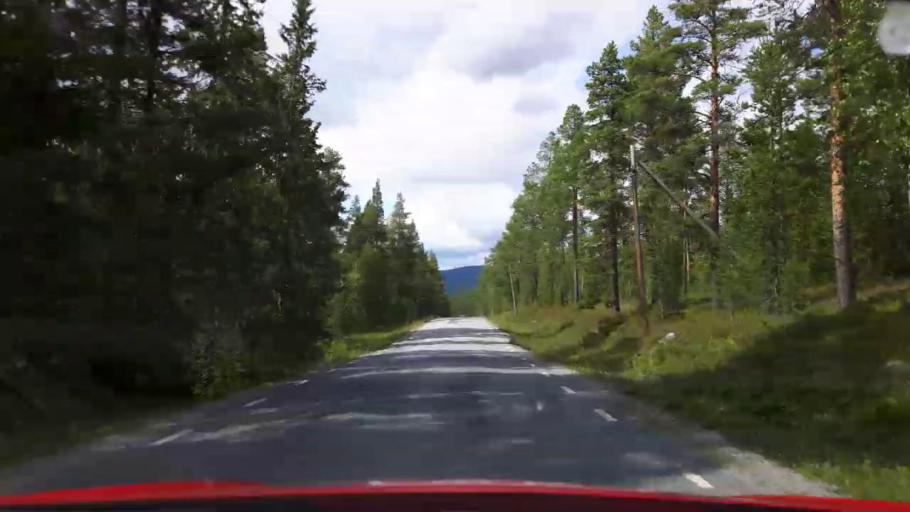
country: NO
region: Hedmark
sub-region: Engerdal
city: Engerdal
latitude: 62.4176
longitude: 12.6992
